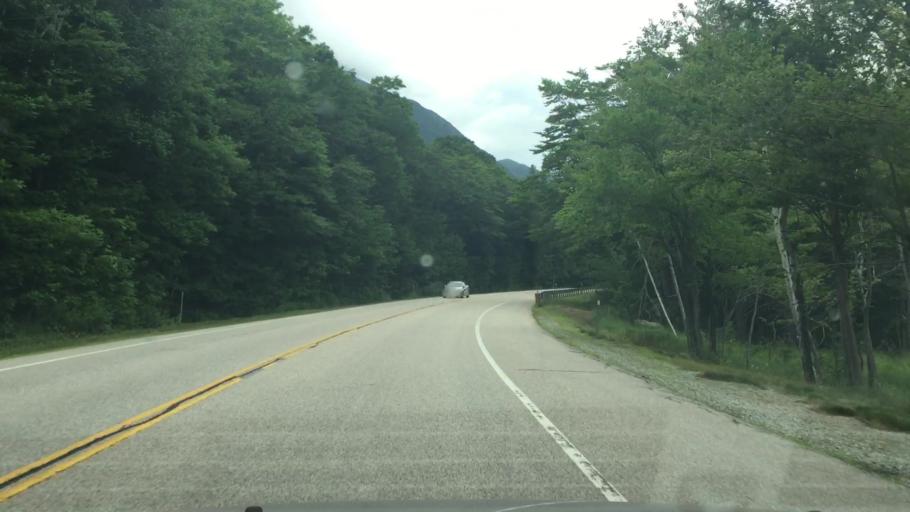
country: US
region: New Hampshire
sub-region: Grafton County
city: Deerfield
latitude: 44.1727
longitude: -71.3929
